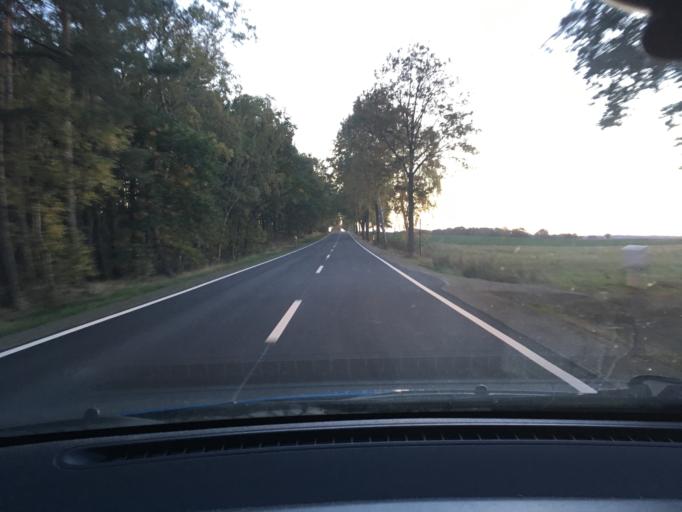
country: DE
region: Lower Saxony
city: Neetze
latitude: 53.2501
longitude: 10.5992
